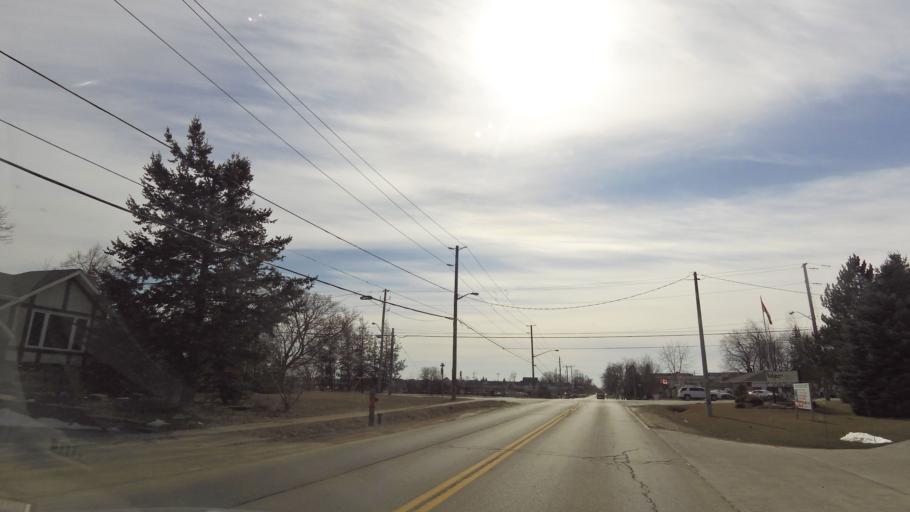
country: CA
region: Ontario
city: Burlington
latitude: 43.3388
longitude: -79.9022
